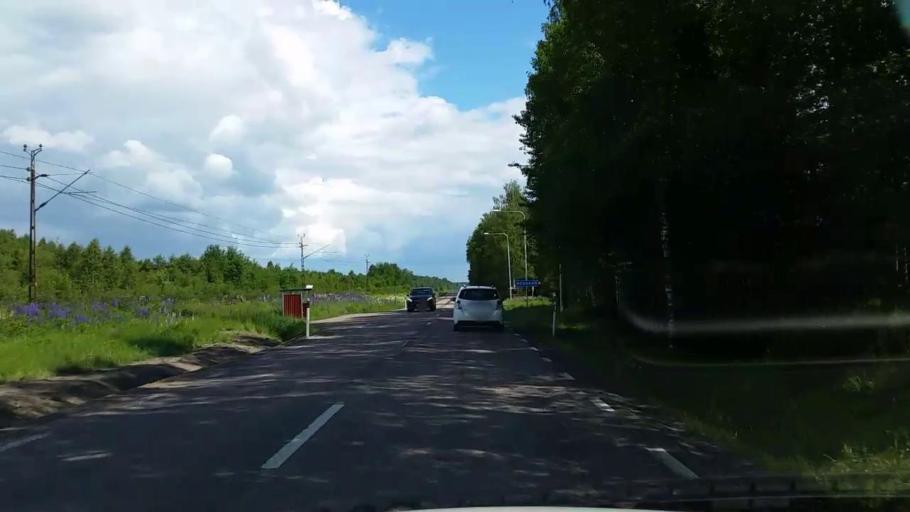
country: SE
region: Dalarna
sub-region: Avesta Kommun
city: Avesta
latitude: 60.1486
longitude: 16.2347
